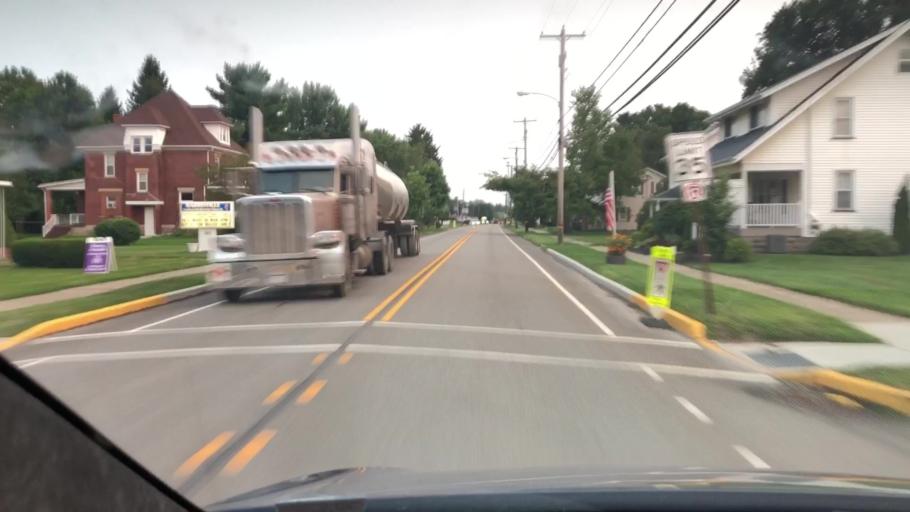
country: US
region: Pennsylvania
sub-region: Mercer County
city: Grove City
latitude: 41.1347
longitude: -80.0090
